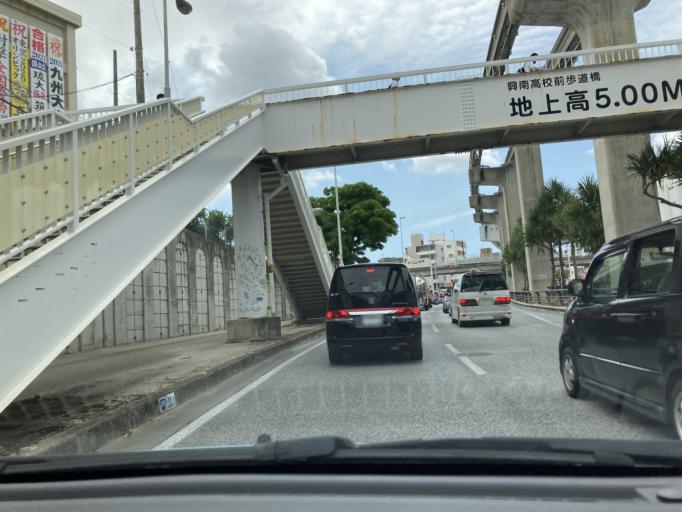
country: JP
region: Okinawa
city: Naha-shi
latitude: 26.2287
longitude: 127.7022
